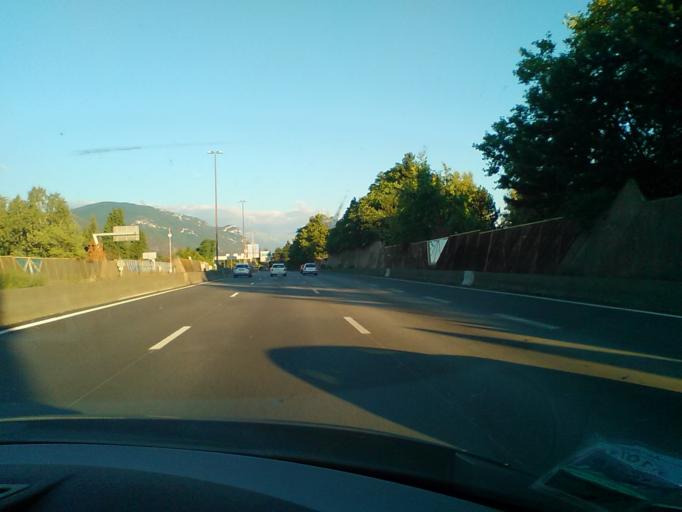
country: FR
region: Rhone-Alpes
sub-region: Departement de la Savoie
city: Chambery
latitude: 45.5711
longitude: 5.9372
